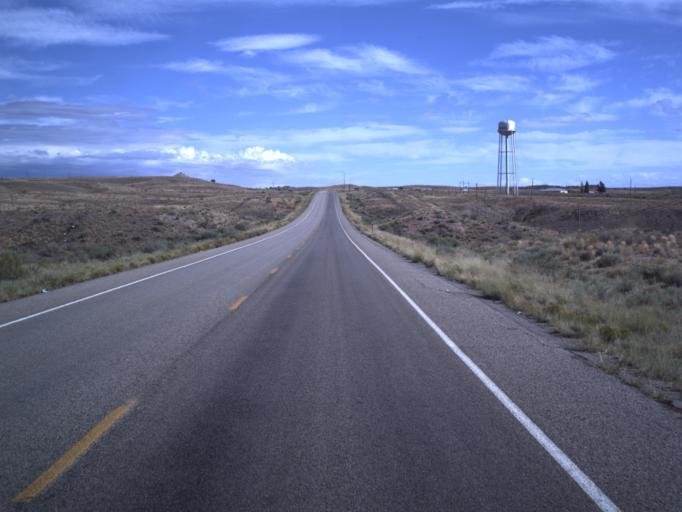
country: US
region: Colorado
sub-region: Montezuma County
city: Towaoc
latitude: 37.2024
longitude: -109.1574
